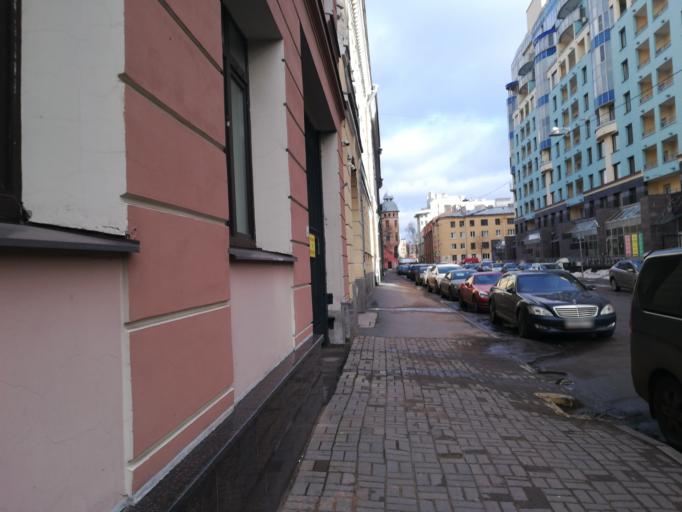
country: RU
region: St.-Petersburg
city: Petrogradka
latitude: 59.9600
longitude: 30.3206
